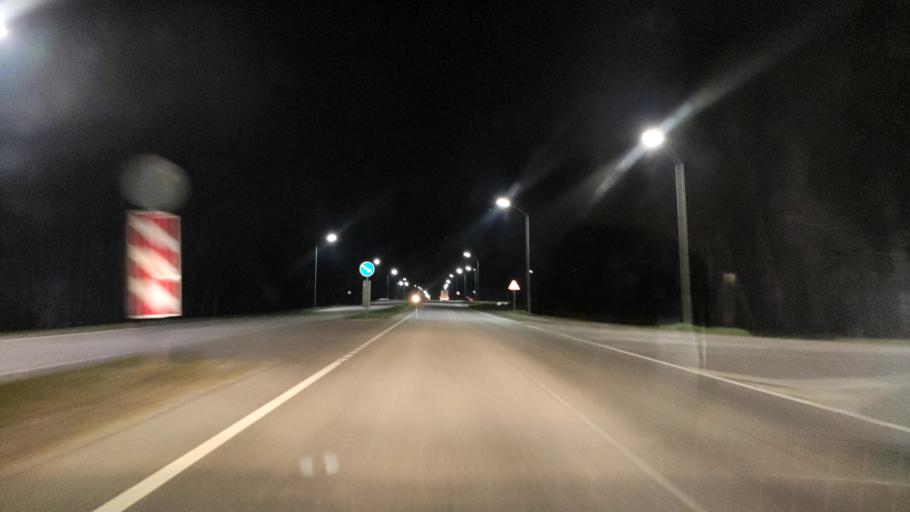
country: RU
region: Belgorod
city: Staryy Oskol
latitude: 51.3641
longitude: 37.8399
